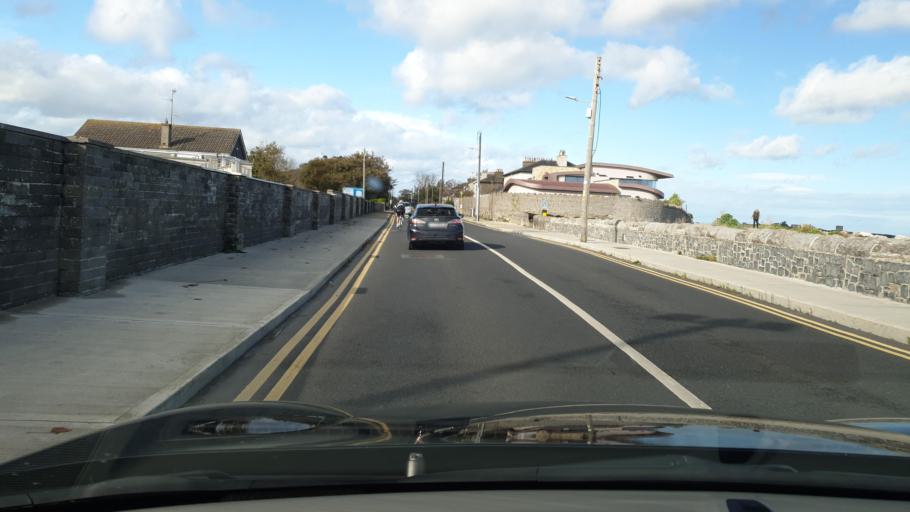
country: IE
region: Leinster
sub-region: Fingal County
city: Skerries
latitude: 53.5721
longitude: -6.1008
